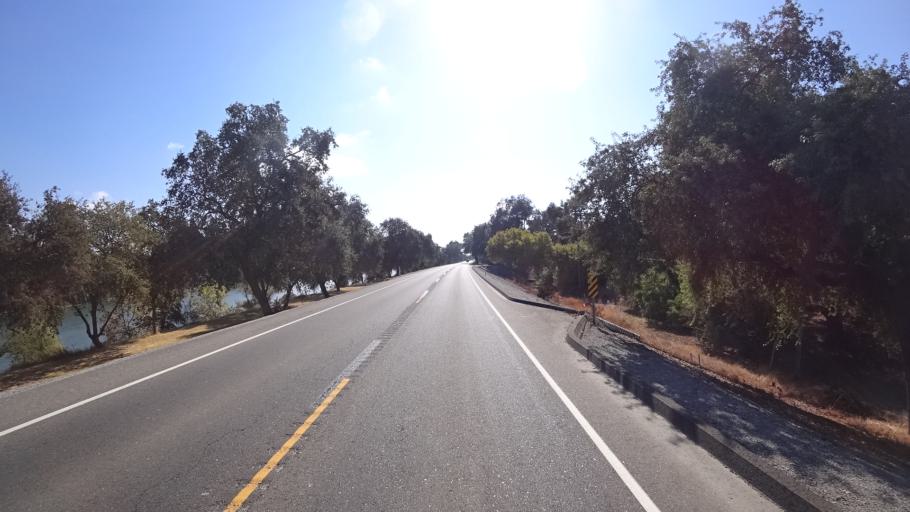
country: US
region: California
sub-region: Yolo County
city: West Sacramento
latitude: 38.6383
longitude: -121.5651
